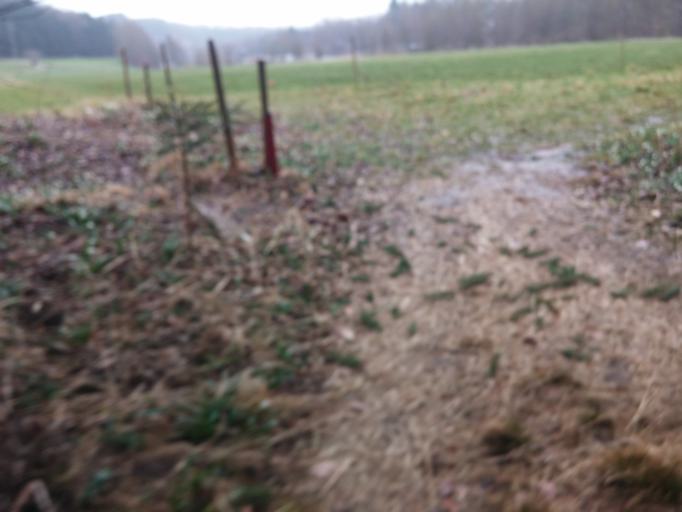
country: DE
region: Bavaria
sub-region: Swabia
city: Kronburg
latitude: 47.8706
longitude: 10.1734
